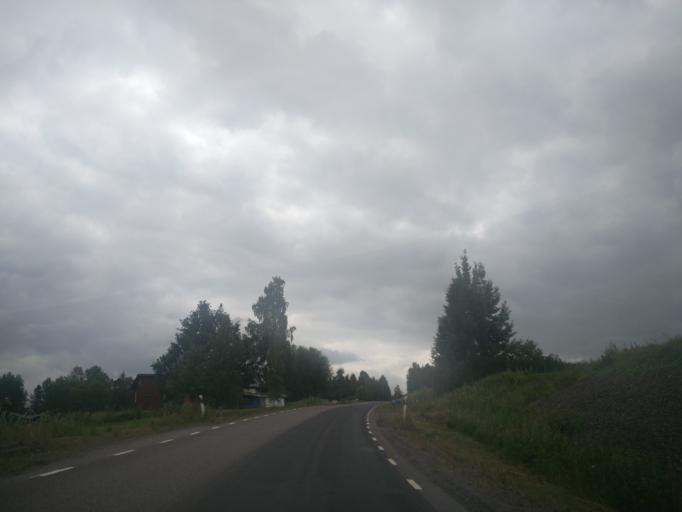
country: SE
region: Vaermland
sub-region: Torsby Kommun
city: Torsby
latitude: 59.9256
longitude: 12.8963
